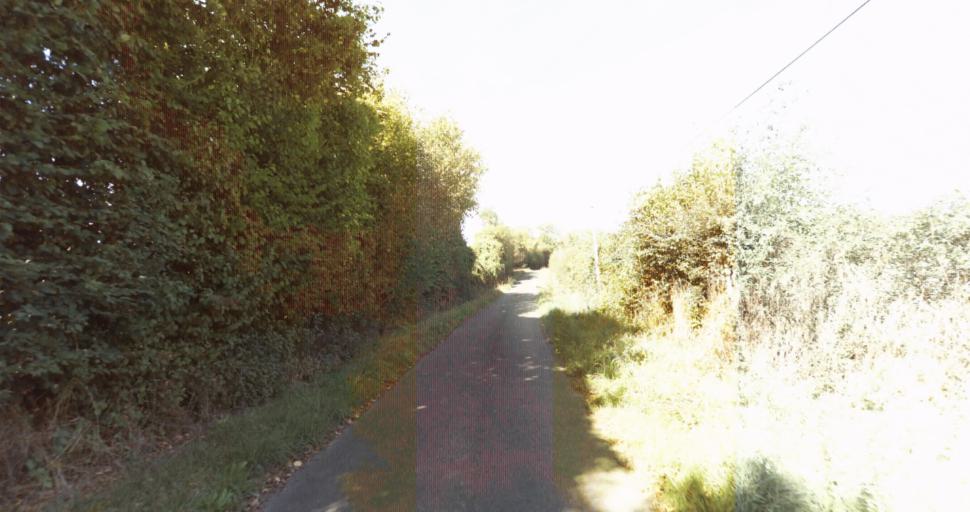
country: FR
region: Lower Normandy
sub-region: Departement de l'Orne
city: Gace
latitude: 48.7564
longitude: 0.2695
